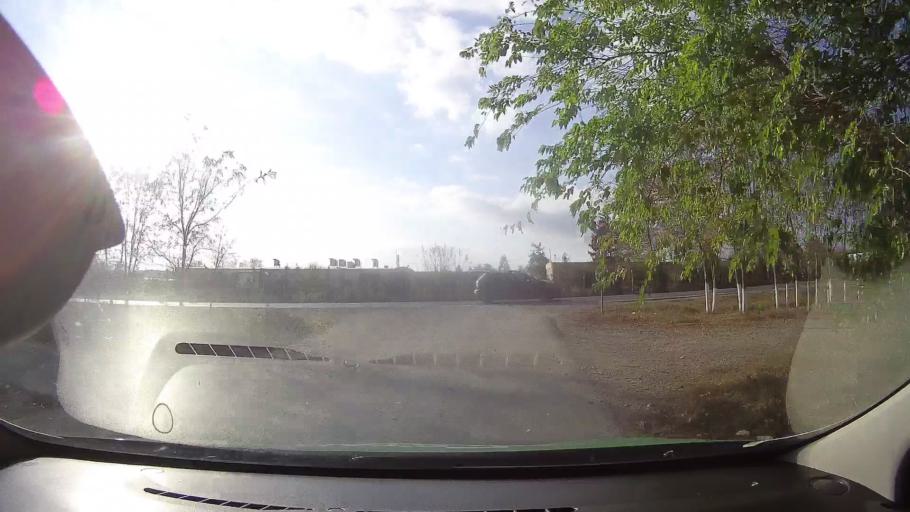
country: RO
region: Constanta
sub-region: Comuna Lumina
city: Lumina
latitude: 44.2875
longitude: 28.5569
